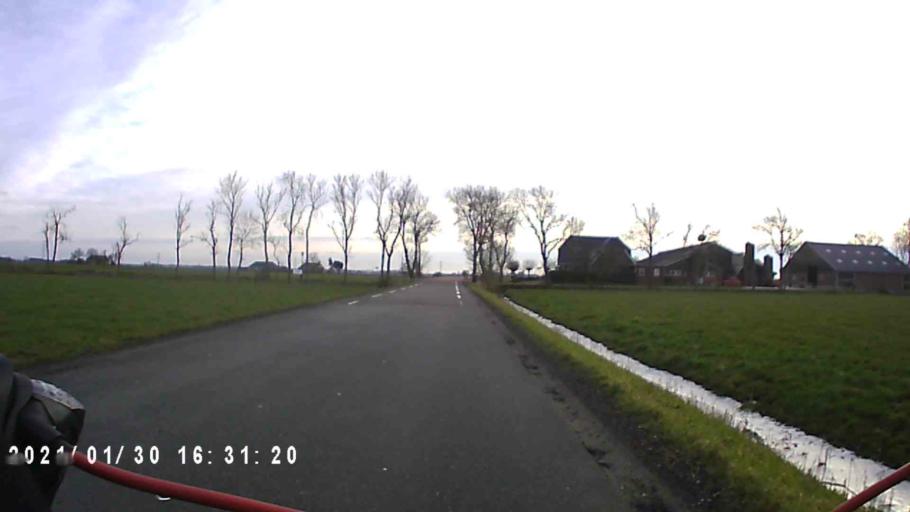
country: NL
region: Groningen
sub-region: Gemeente Zuidhorn
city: Zuidhorn
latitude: 53.2173
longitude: 6.3890
